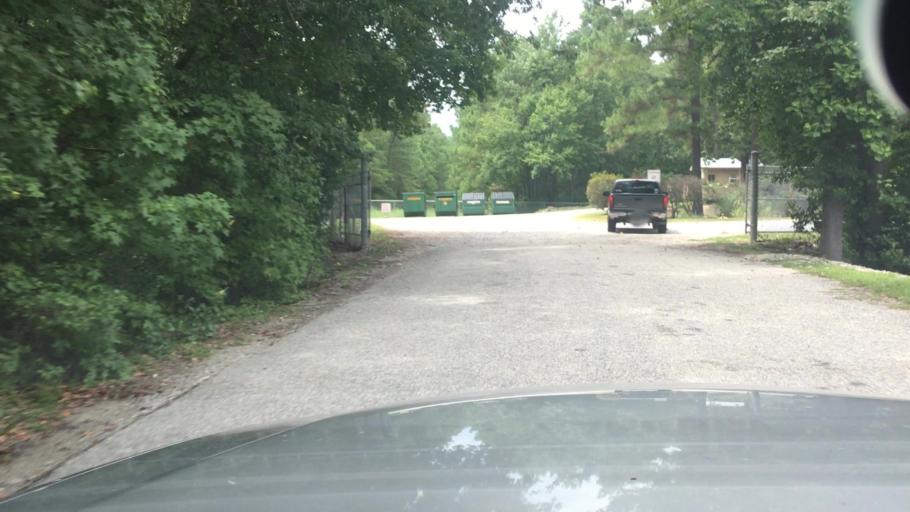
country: US
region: North Carolina
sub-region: Cumberland County
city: Hope Mills
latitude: 34.9623
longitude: -78.8986
